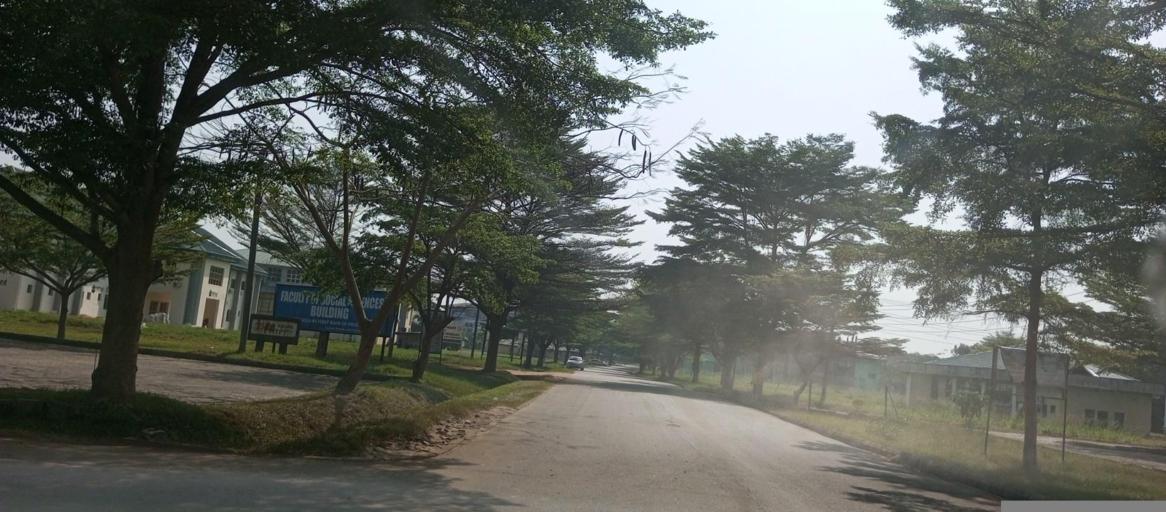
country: NG
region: Rivers
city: Emuoha
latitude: 4.9068
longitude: 6.9175
